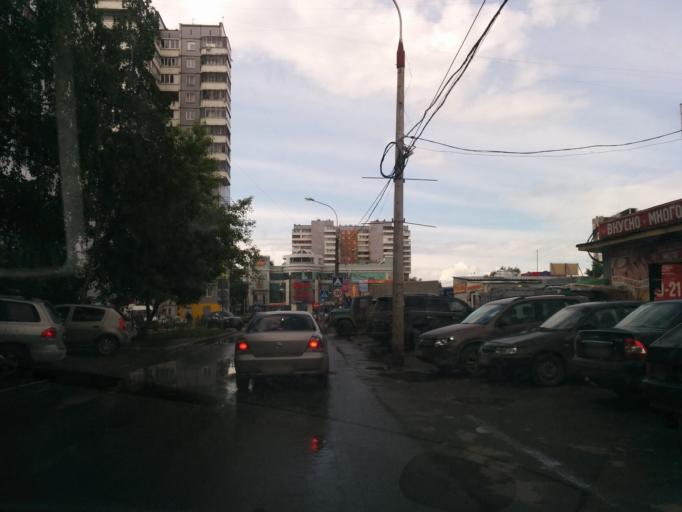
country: RU
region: Perm
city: Kondratovo
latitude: 57.9969
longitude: 56.1558
